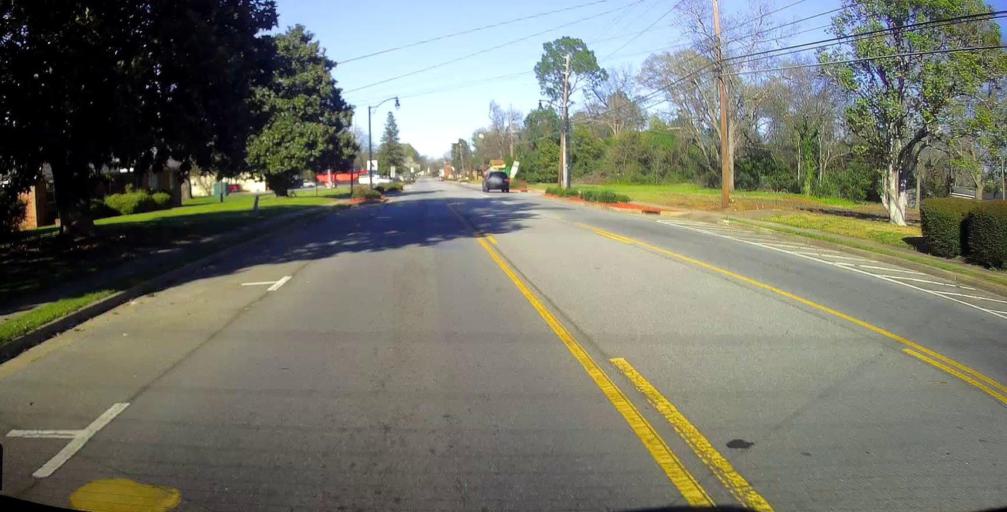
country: US
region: Georgia
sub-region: Peach County
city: Fort Valley
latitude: 32.5423
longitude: -83.8950
